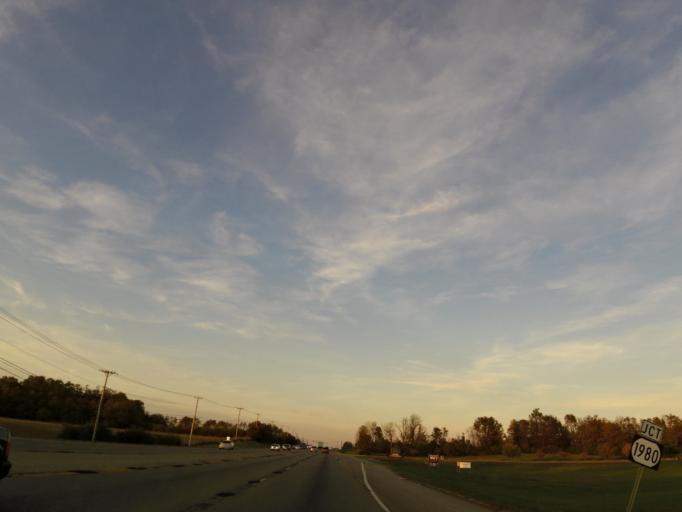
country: US
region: Kentucky
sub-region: Fayette County
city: Monticello
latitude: 37.9474
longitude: -84.5434
